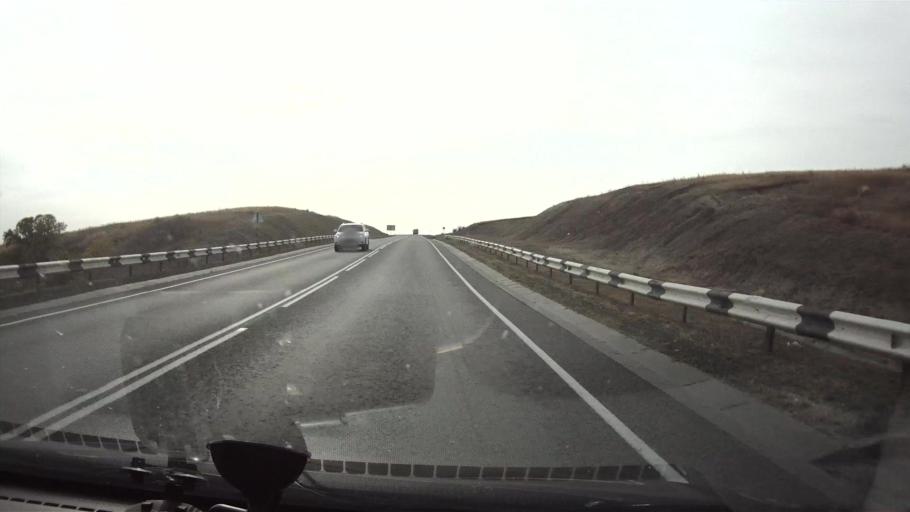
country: RU
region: Saratov
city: Sennoy
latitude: 52.1396
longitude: 46.8838
